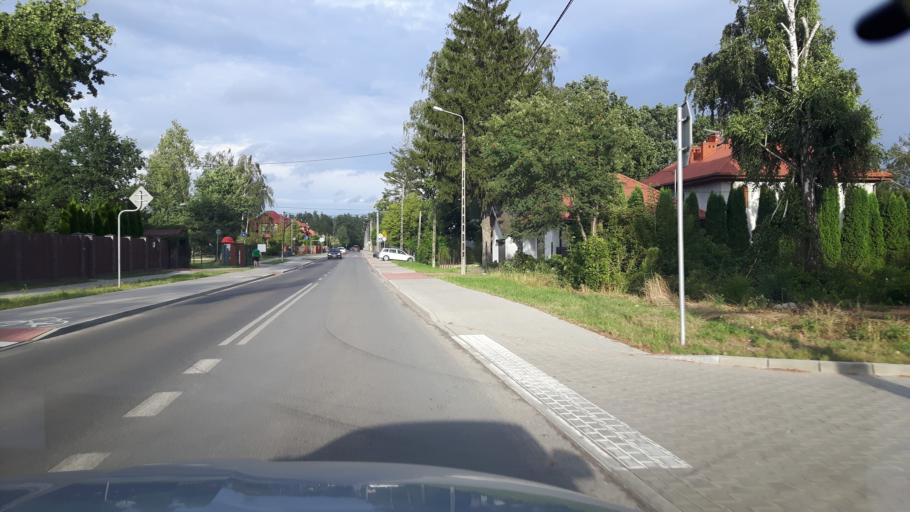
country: PL
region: Masovian Voivodeship
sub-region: Powiat wolominski
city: Marki
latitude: 52.3287
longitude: 21.1312
